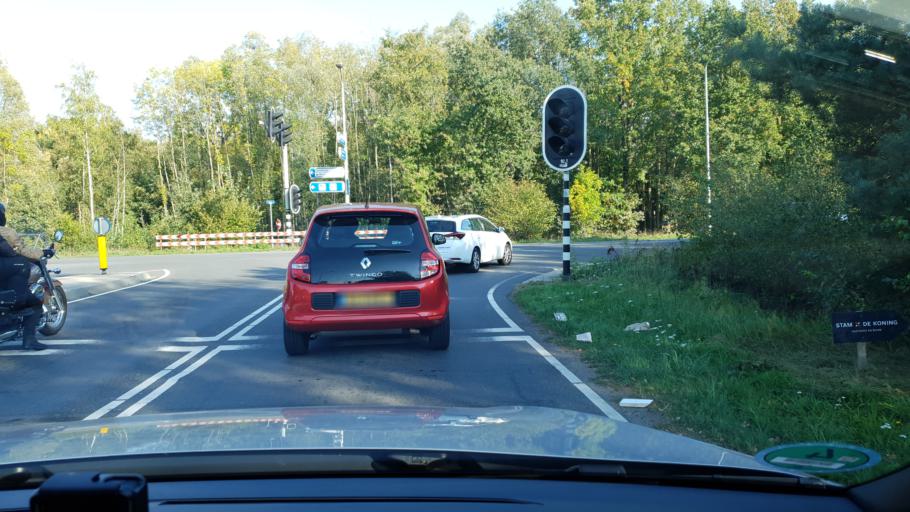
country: NL
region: North Brabant
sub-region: Gemeente Best
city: Best
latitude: 51.4877
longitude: 5.3897
